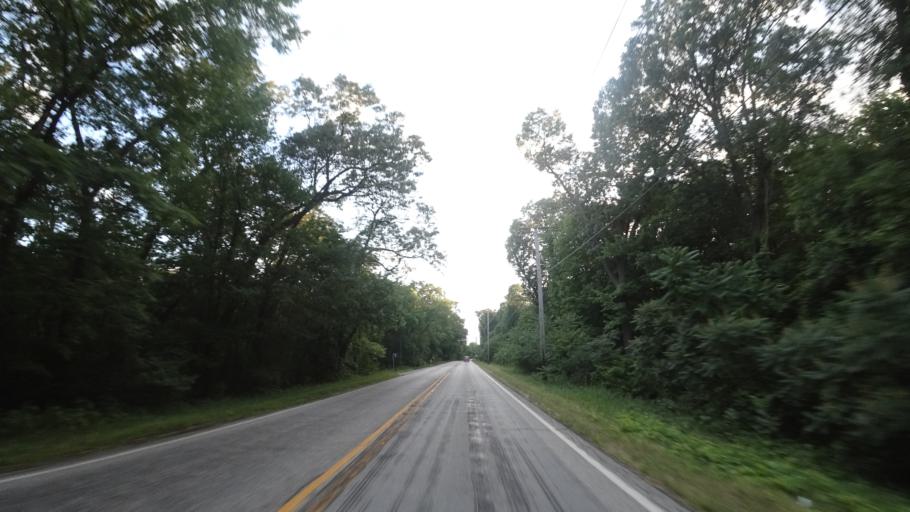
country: US
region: Indiana
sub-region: Porter County
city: Porter
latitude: 41.6392
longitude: -87.0714
